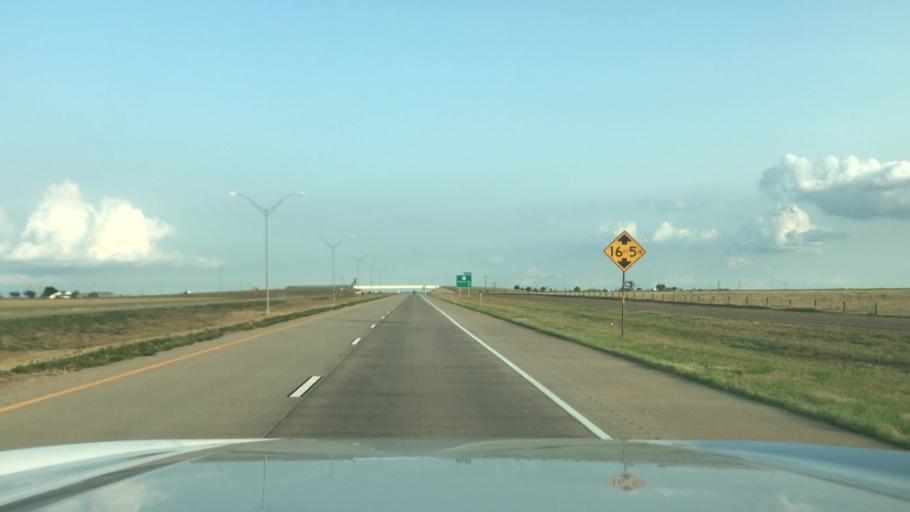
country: US
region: Texas
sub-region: Hale County
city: Seth Ward
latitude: 34.3512
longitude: -101.7523
